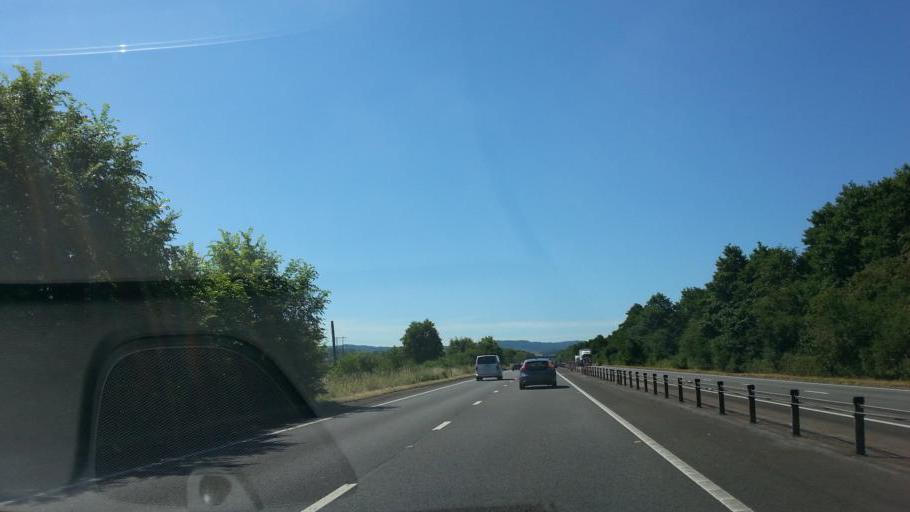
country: GB
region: Wales
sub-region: Monmouthshire
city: Llangwm
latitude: 51.7513
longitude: -2.8421
